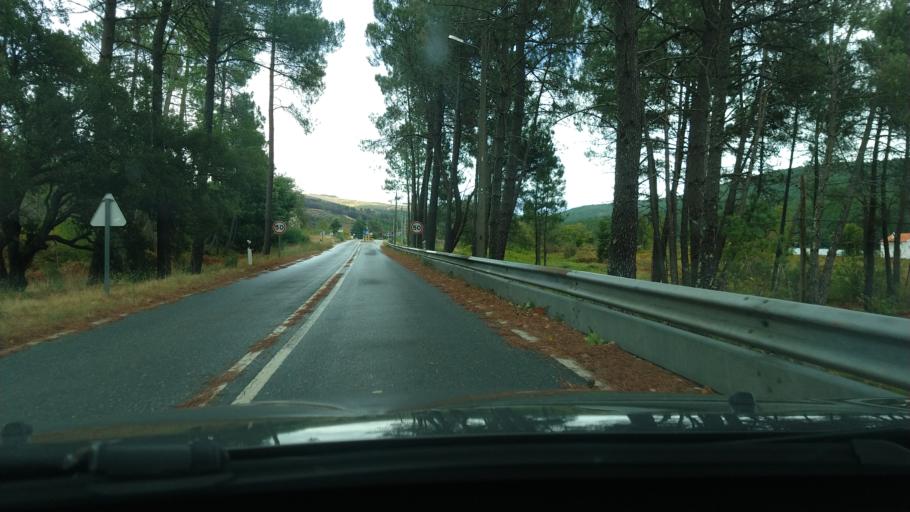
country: PT
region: Castelo Branco
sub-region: Covilha
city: Covilha
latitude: 40.2376
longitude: -7.5906
